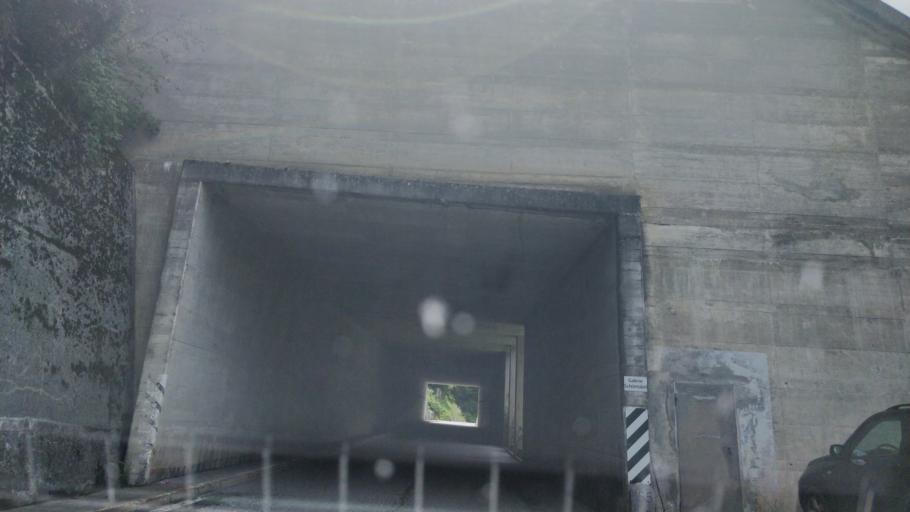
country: CH
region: Grisons
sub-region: Surselva District
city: Ilanz
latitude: 46.6570
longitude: 9.1906
